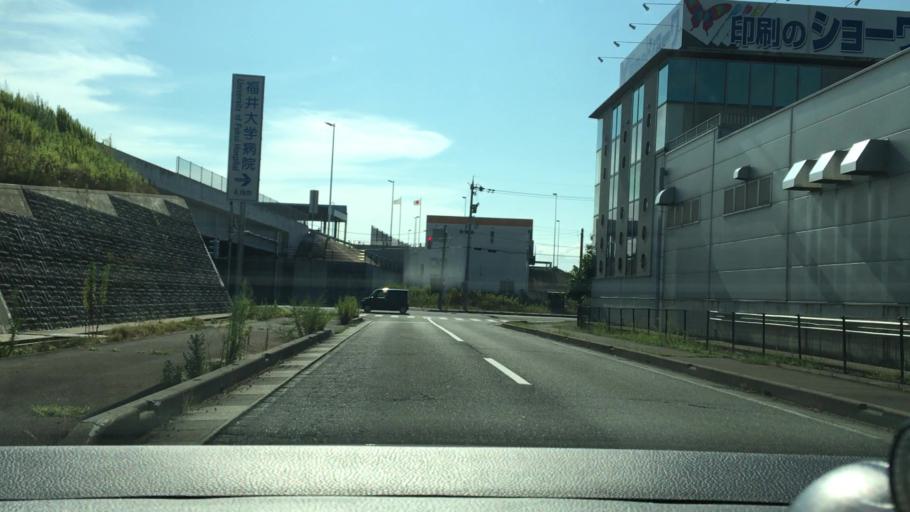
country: JP
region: Fukui
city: Fukui-shi
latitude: 36.0864
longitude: 136.2837
